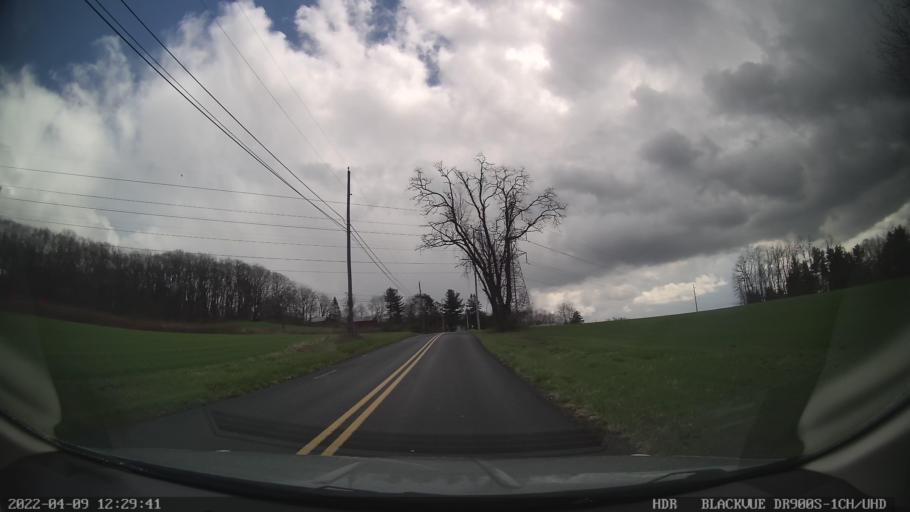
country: US
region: Pennsylvania
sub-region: Berks County
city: Kutztown
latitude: 40.4667
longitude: -75.7646
